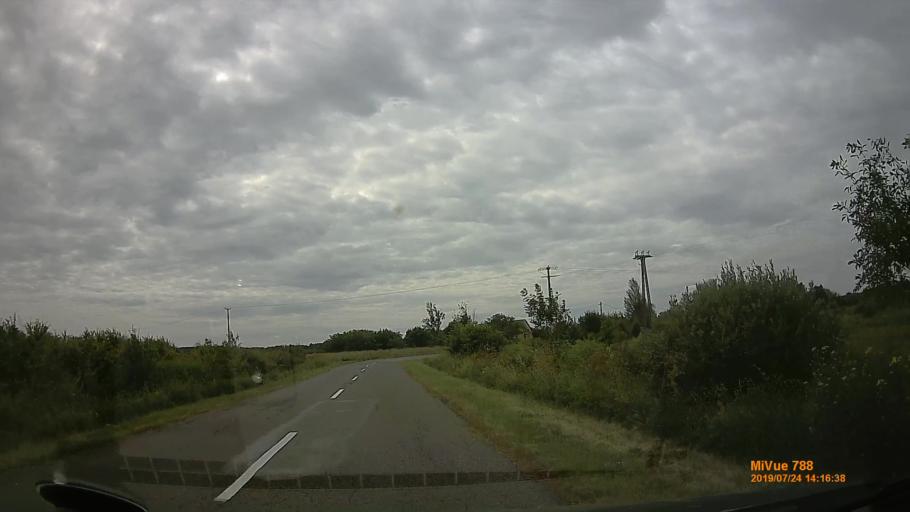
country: HU
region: Szabolcs-Szatmar-Bereg
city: Mandok
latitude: 48.3149
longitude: 22.2921
